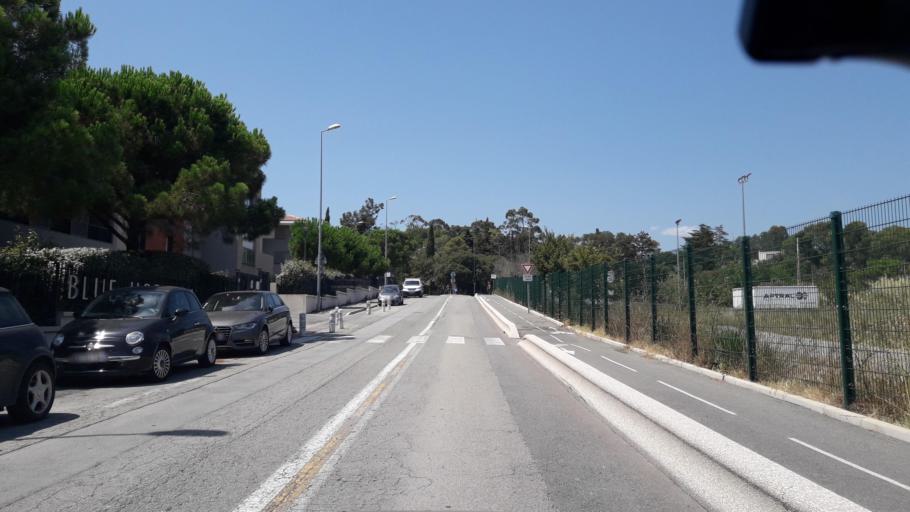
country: FR
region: Provence-Alpes-Cote d'Azur
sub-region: Departement du Var
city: Frejus
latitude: 43.4465
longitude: 6.7532
